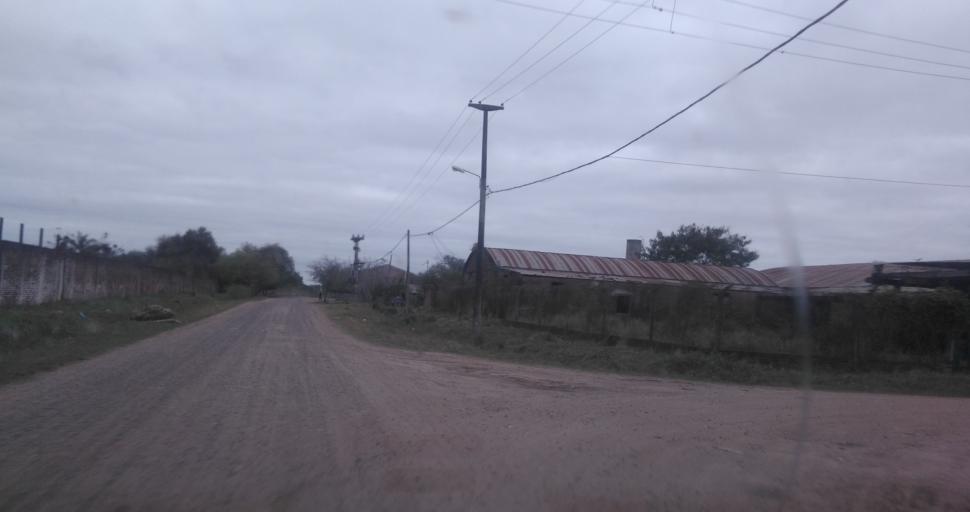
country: AR
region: Chaco
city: Fontana
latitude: -27.4335
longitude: -59.0260
